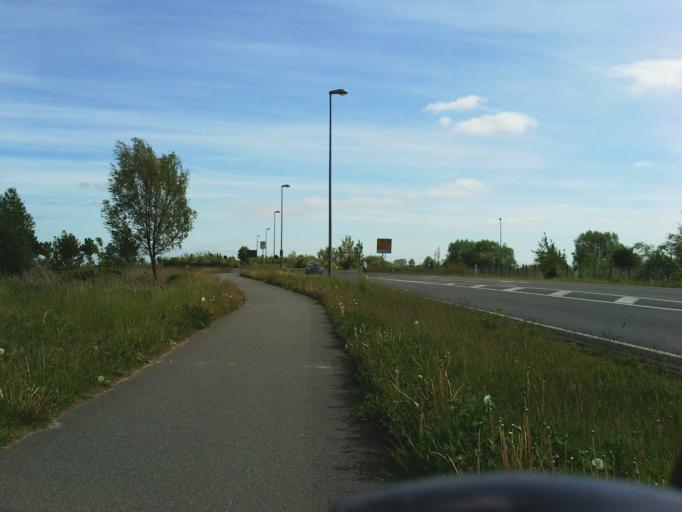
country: DE
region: Mecklenburg-Vorpommern
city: Papendorf
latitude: 54.0575
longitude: 12.1174
